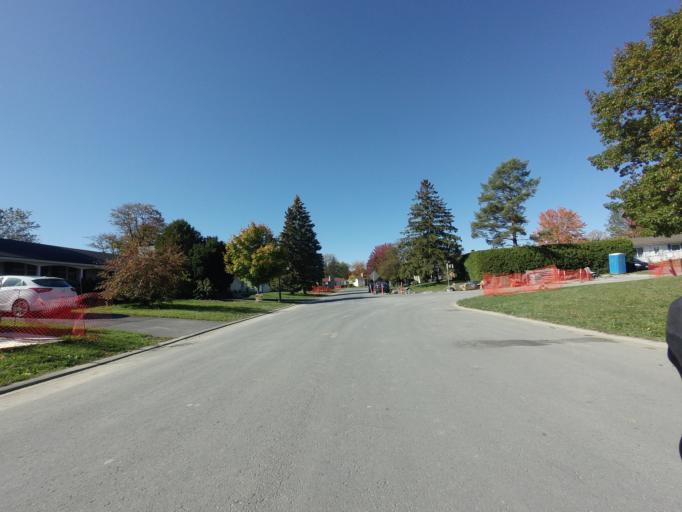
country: CA
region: Ontario
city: Bells Corners
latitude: 45.2973
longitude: -75.8769
